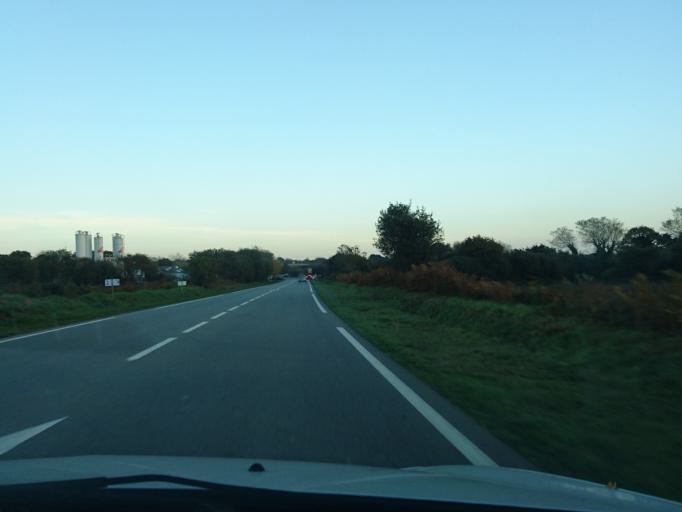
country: FR
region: Brittany
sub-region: Departement du Finistere
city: Saint-Renan
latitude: 48.4302
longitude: -4.6023
